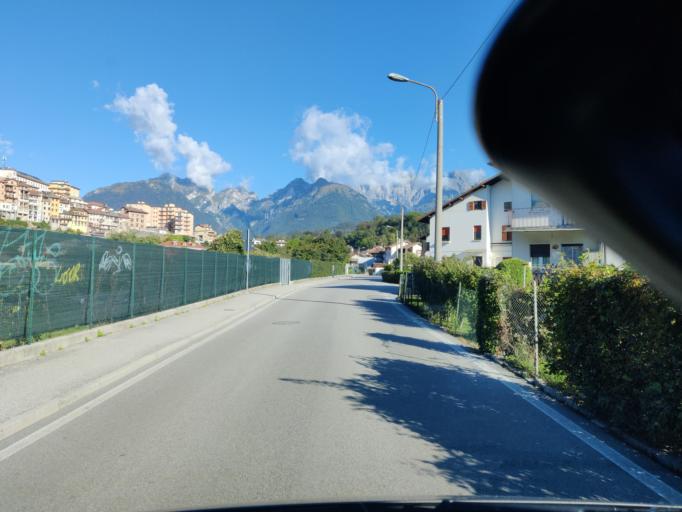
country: IT
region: Veneto
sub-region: Provincia di Belluno
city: Belluno
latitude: 46.1399
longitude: 12.2219
